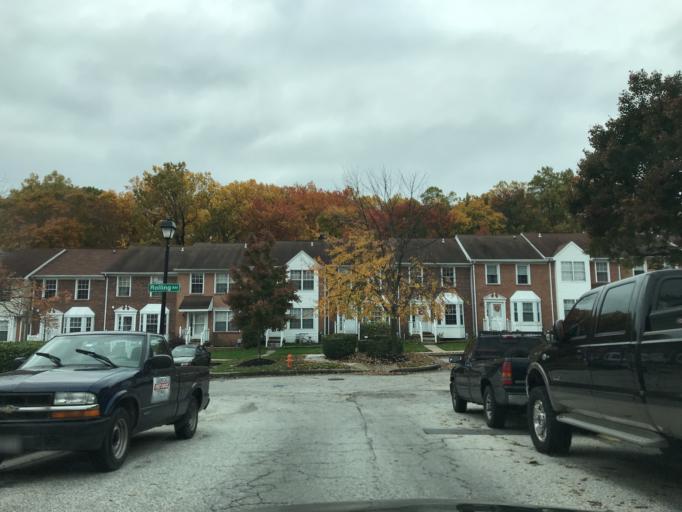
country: US
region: Maryland
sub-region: Baltimore County
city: Overlea
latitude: 39.3768
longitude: -76.5161
